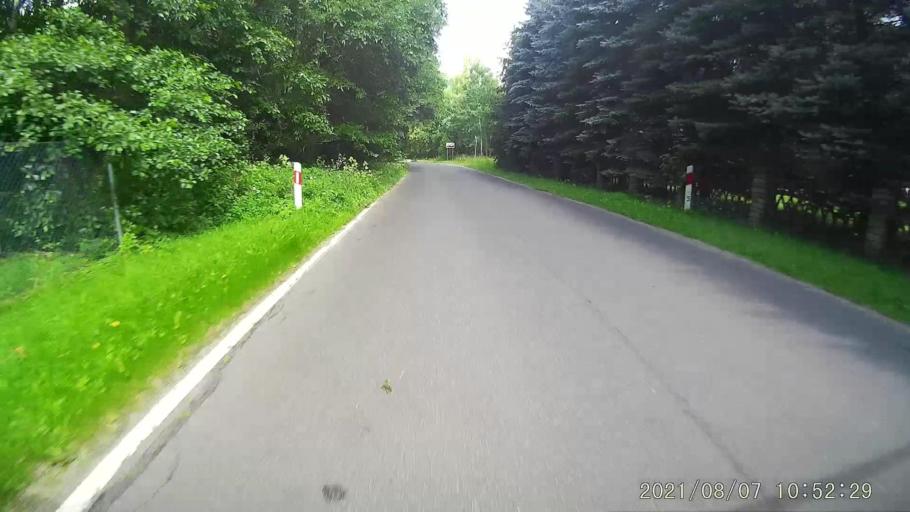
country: CZ
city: Rokytnice v Orlickych Horach
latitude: 50.2818
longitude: 16.4745
